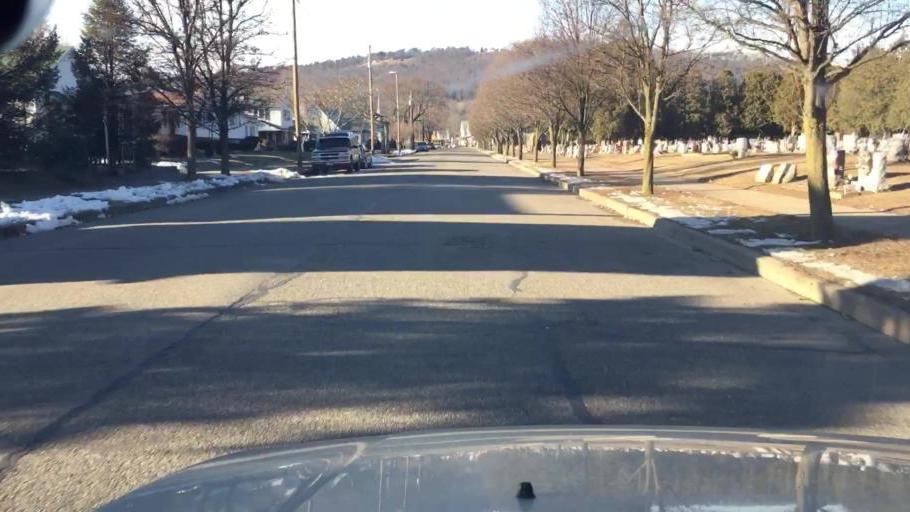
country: US
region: Pennsylvania
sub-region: Columbia County
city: Berwick
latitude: 41.0660
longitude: -76.2358
